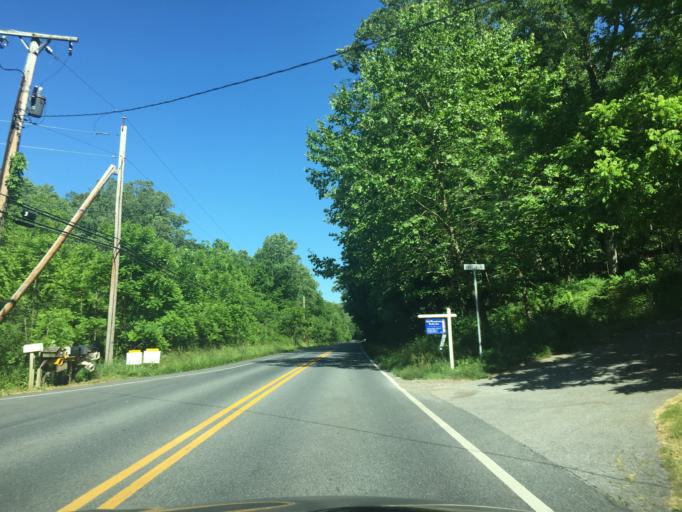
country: US
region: Maryland
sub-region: Carroll County
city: Westminster
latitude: 39.5692
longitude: -76.9561
